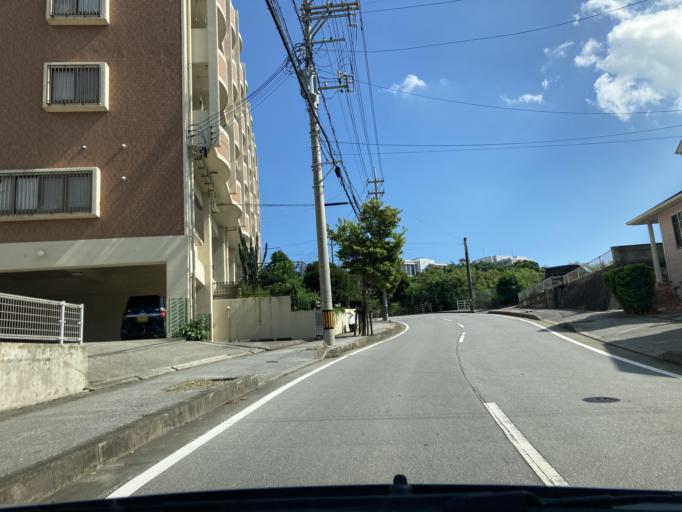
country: JP
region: Okinawa
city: Ginowan
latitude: 26.2442
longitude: 127.7557
